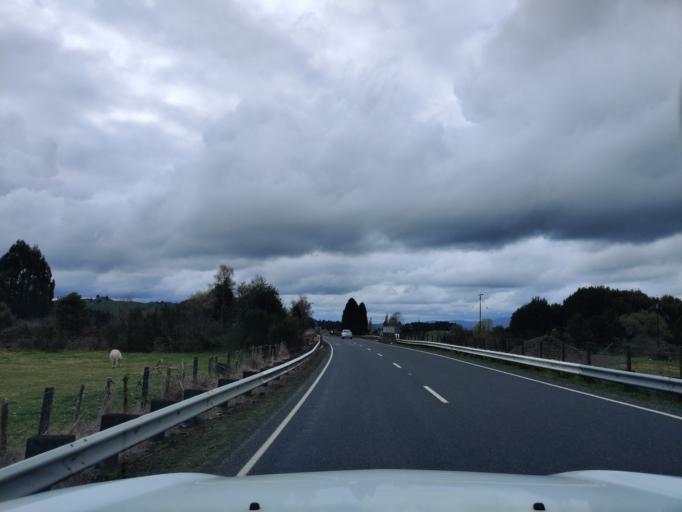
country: NZ
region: Waikato
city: Turangi
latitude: -38.9911
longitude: 175.3788
